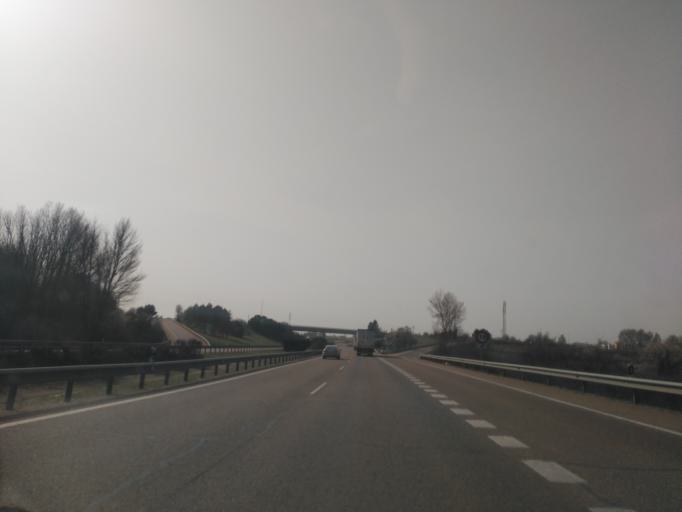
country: ES
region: Castille and Leon
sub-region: Provincia de Valladolid
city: Valladolid
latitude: 41.6806
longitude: -4.7370
